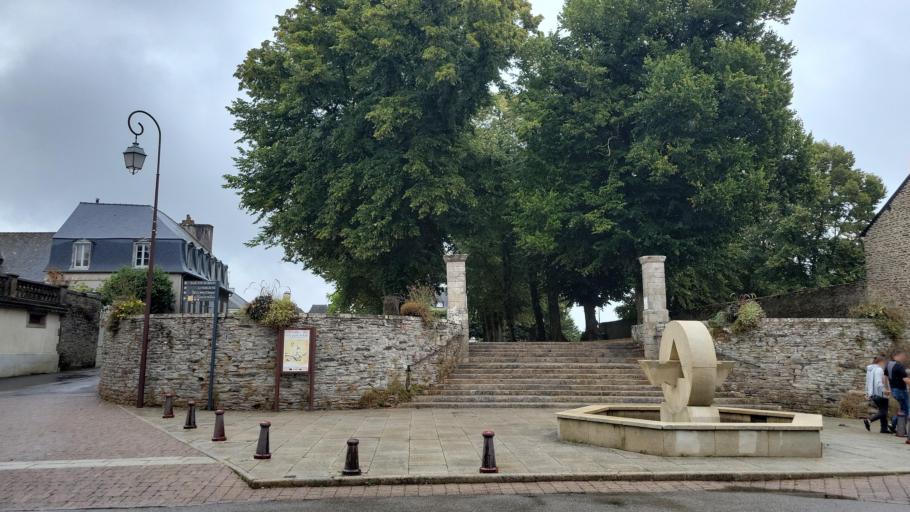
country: FR
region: Brittany
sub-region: Departement du Morbihan
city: Josselin
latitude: 47.9555
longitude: -2.5477
